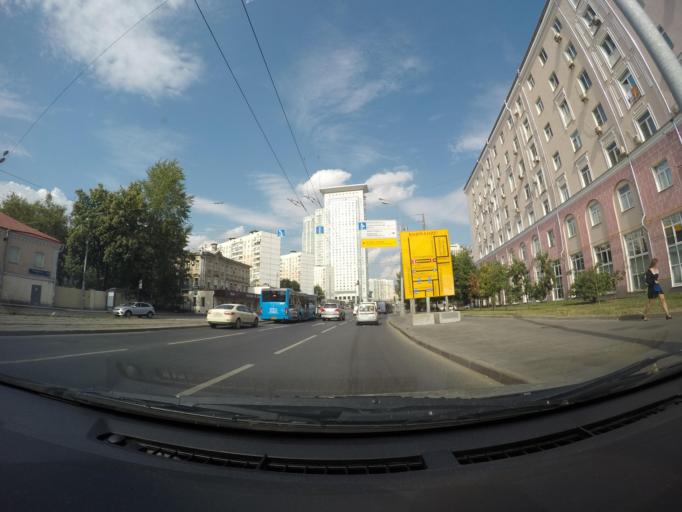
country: RU
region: Moscow
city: Sokol'niki
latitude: 55.7852
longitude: 37.6759
